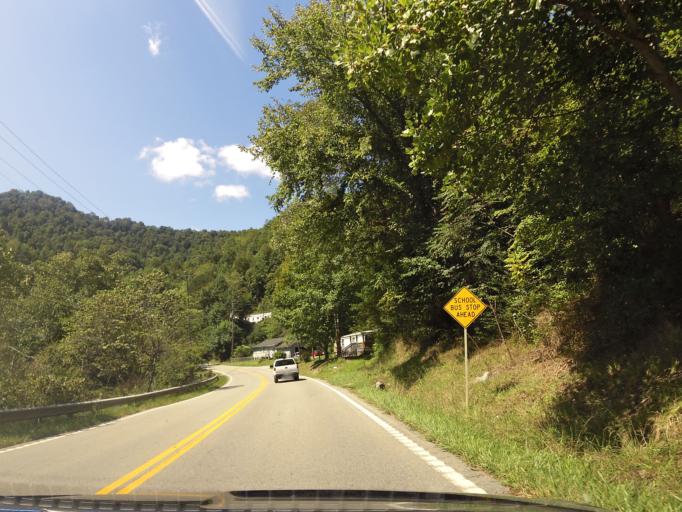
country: US
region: Kentucky
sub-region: Leslie County
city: Hyden
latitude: 37.0745
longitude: -83.3998
